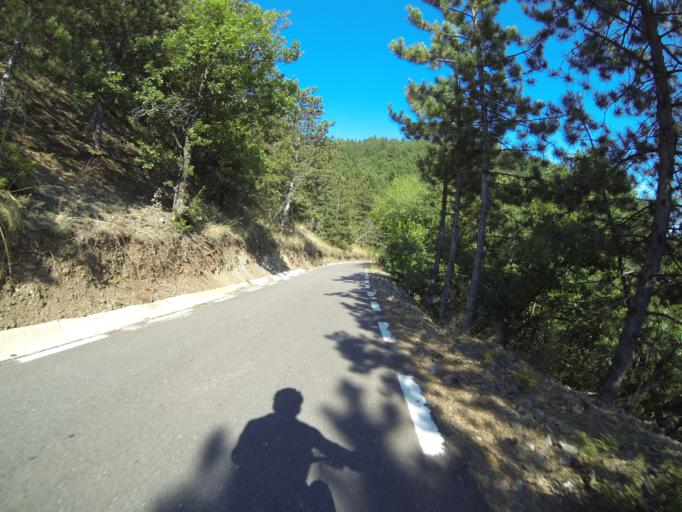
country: RO
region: Mehedinti
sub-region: Comuna Svinita
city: Svinita
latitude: 44.5421
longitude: 22.1880
